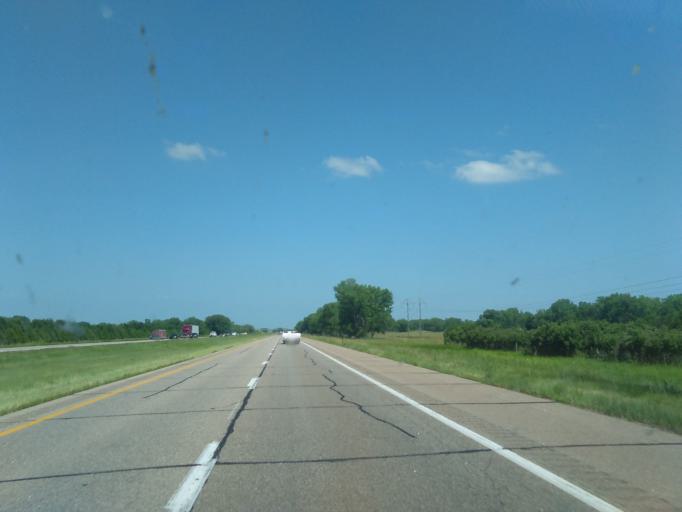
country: US
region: Nebraska
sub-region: Buffalo County
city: Kearney
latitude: 40.6826
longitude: -99.3020
